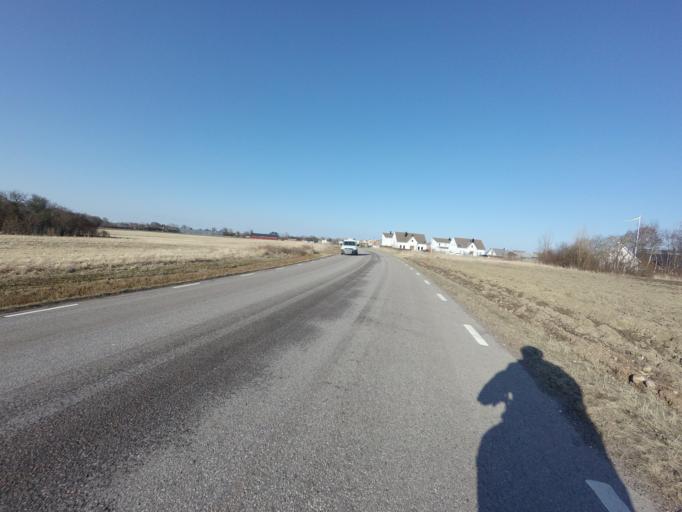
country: SE
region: Skane
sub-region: Hoganas Kommun
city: Hoganas
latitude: 56.1476
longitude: 12.5904
